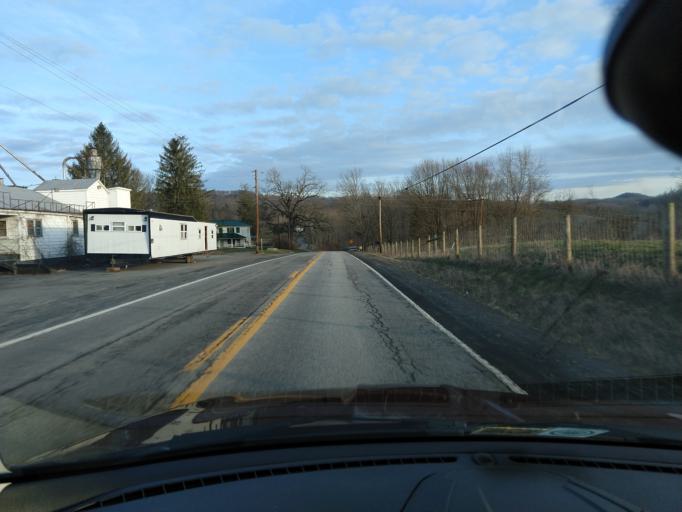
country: US
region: West Virginia
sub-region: Greenbrier County
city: Lewisburg
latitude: 37.9716
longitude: -80.3844
